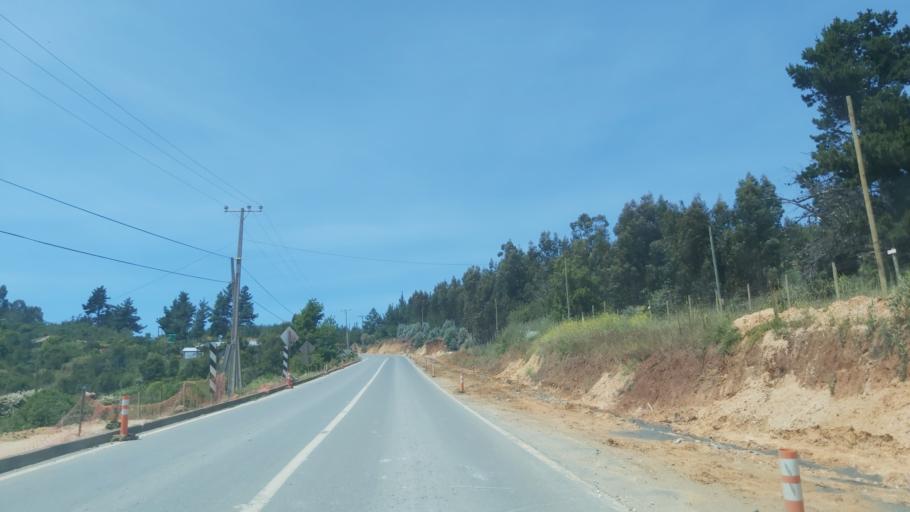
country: CL
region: Maule
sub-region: Provincia de Talca
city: Constitucion
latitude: -35.4431
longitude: -72.4607
